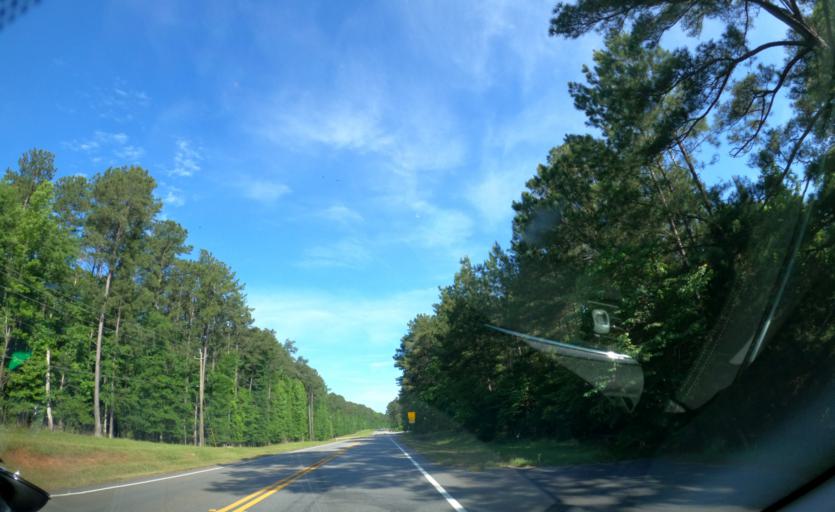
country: US
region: Georgia
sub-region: Columbia County
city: Appling
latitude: 33.6335
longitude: -82.2969
